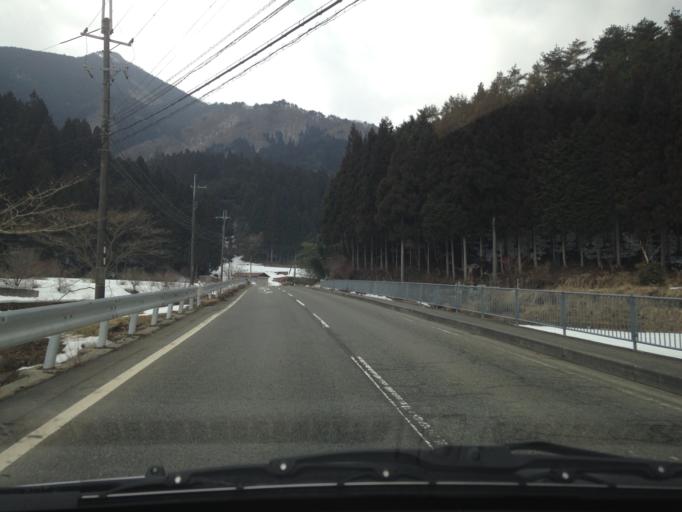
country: JP
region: Hyogo
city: Yamazakicho-nakabirose
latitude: 35.1951
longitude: 134.4370
